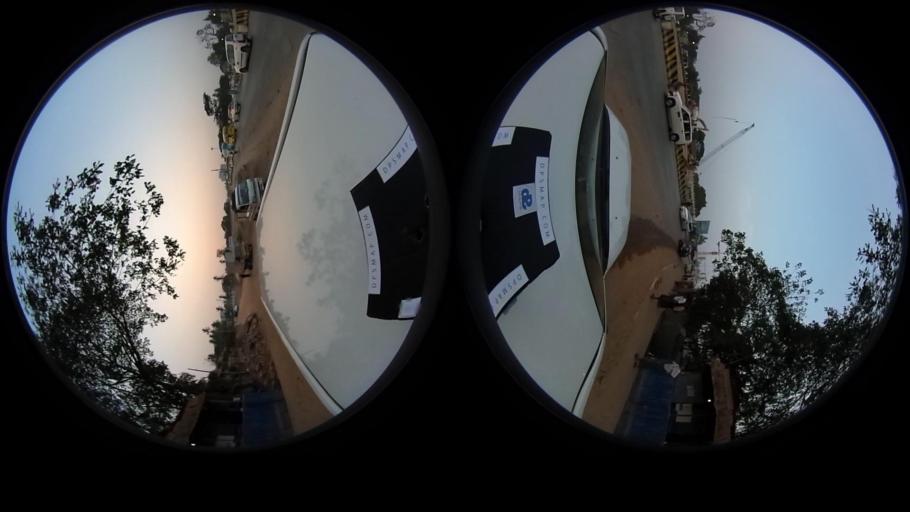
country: MM
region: Yangon
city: Yangon
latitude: 16.7863
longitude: 96.1776
